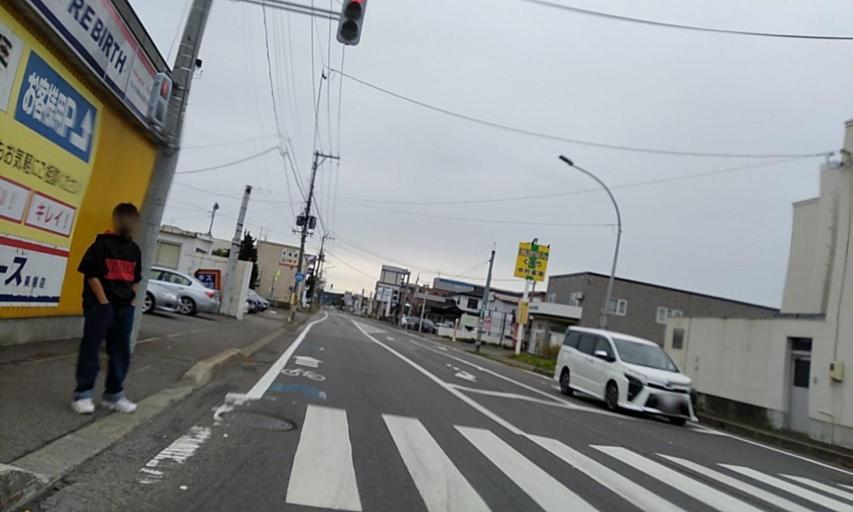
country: JP
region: Hokkaido
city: Bihoro
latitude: 43.8336
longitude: 144.1046
